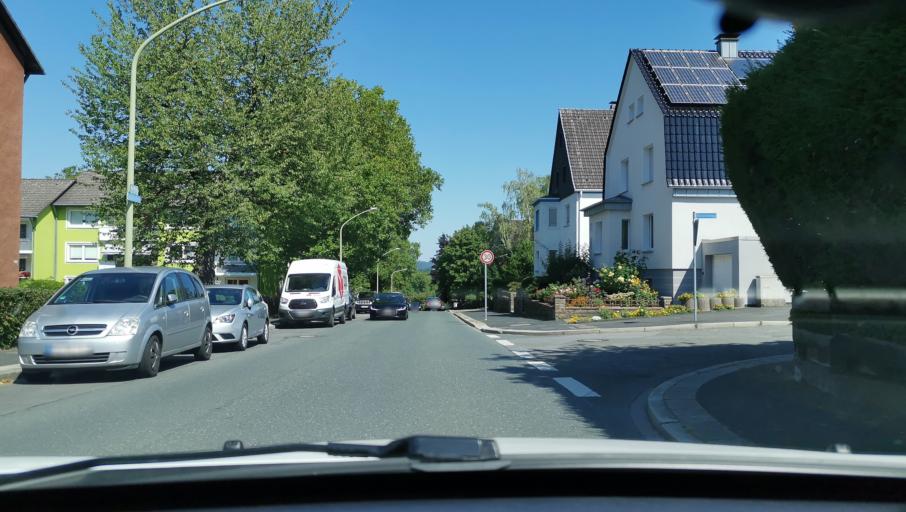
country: DE
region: North Rhine-Westphalia
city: Herdecke
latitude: 51.3804
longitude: 7.4395
